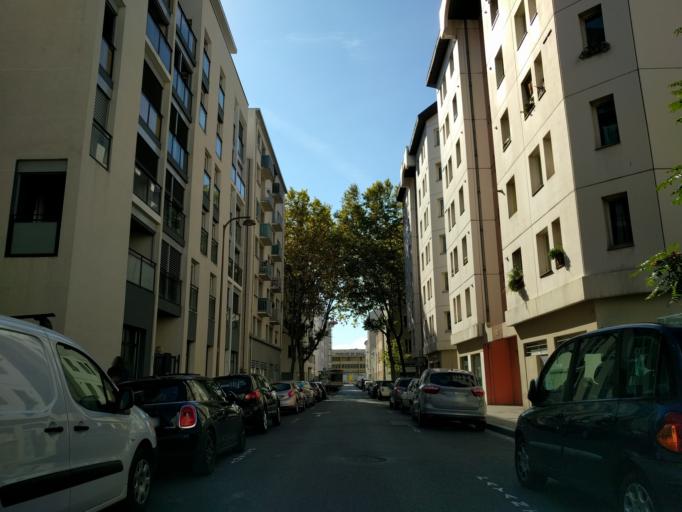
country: FR
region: Rhone-Alpes
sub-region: Departement du Rhone
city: Lyon
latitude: 45.7433
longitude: 4.8243
